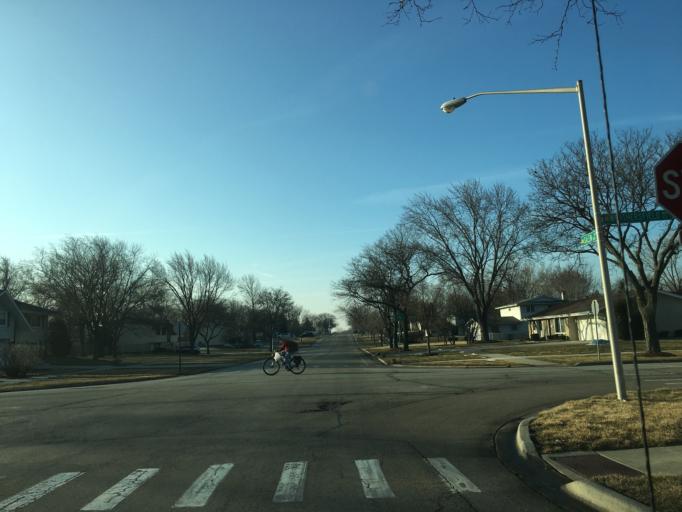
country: US
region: Illinois
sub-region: Cook County
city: Schaumburg
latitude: 42.0181
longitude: -88.0996
